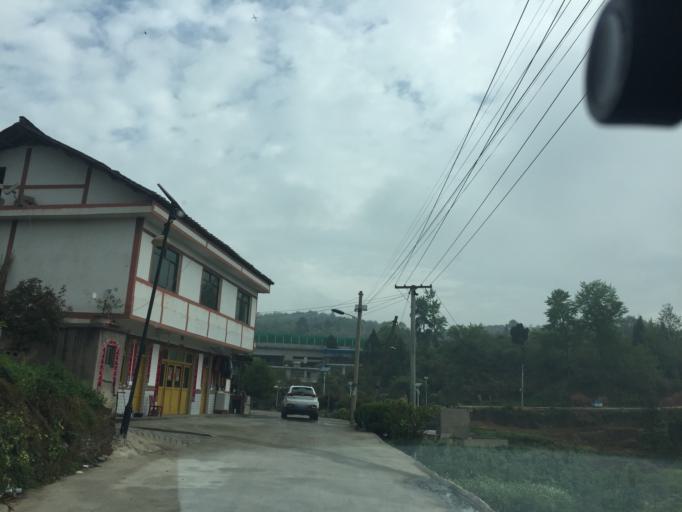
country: CN
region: Guizhou Sheng
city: Guiyang
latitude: 26.8060
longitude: 106.8606
